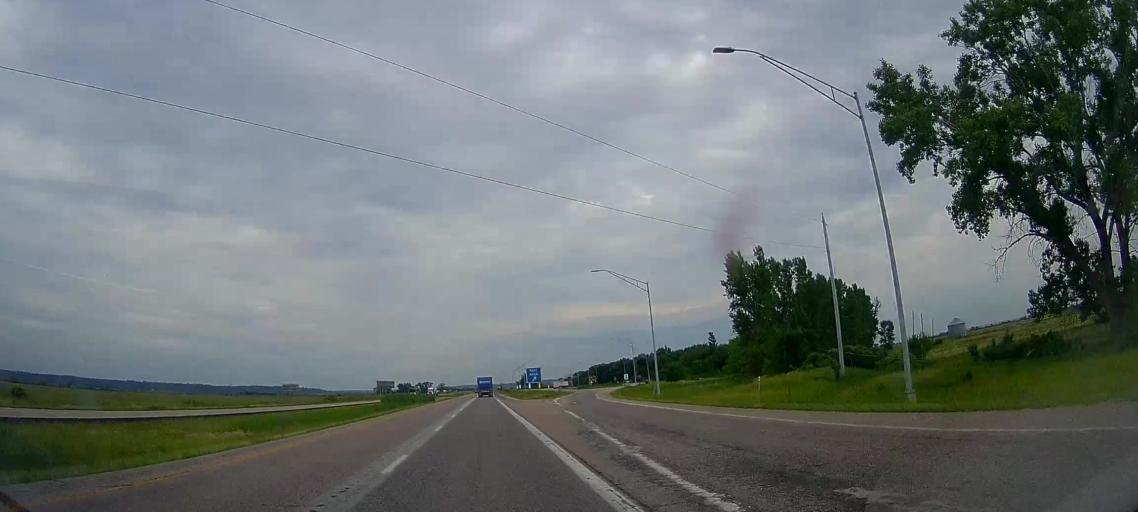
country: US
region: Iowa
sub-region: Harrison County
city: Missouri Valley
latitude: 41.5940
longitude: -95.9551
